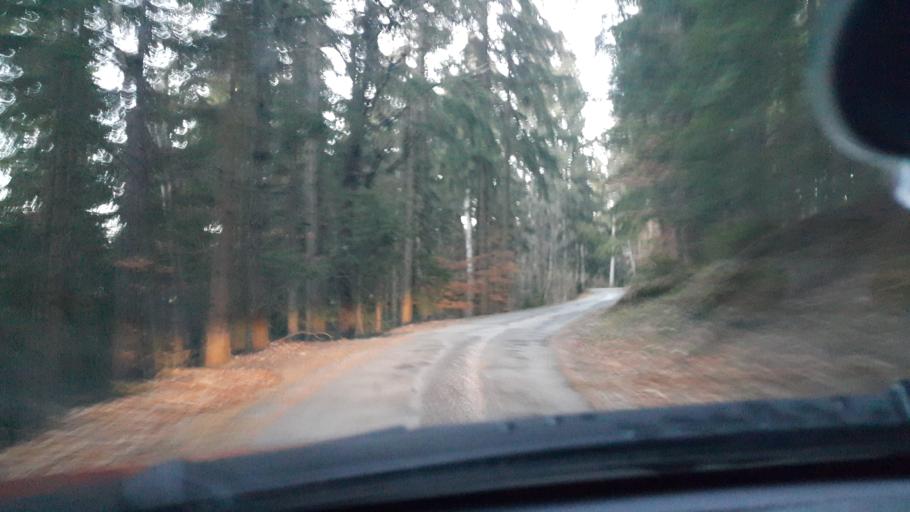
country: AT
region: Styria
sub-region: Politischer Bezirk Graz-Umgebung
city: Stiwoll
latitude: 47.1241
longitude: 15.2202
